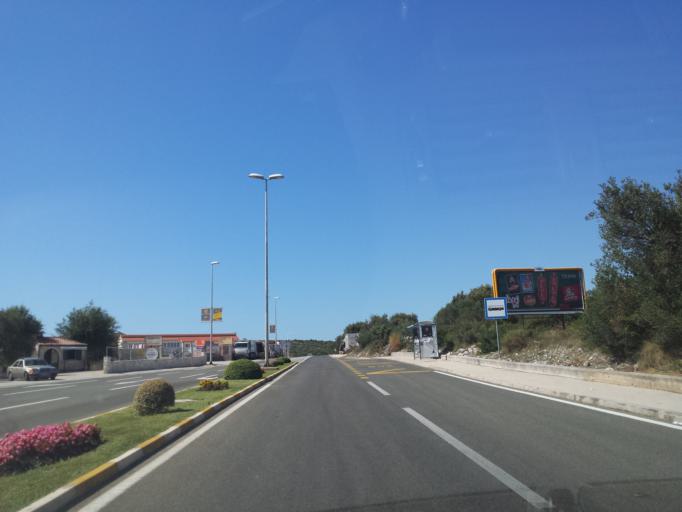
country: HR
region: Sibensko-Kniniska
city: Rogoznica
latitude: 43.5413
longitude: 15.9688
